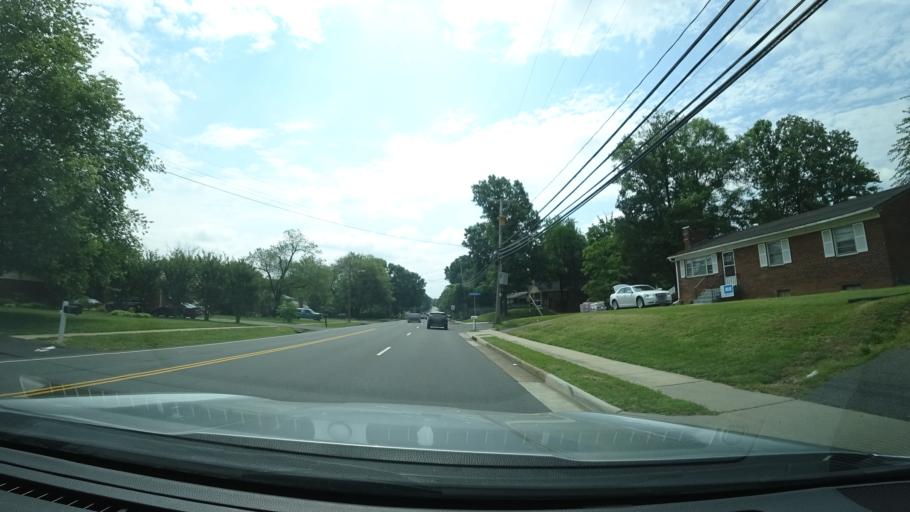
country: US
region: Virginia
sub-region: Loudoun County
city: Oak Grove
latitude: 38.9738
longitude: -77.4022
